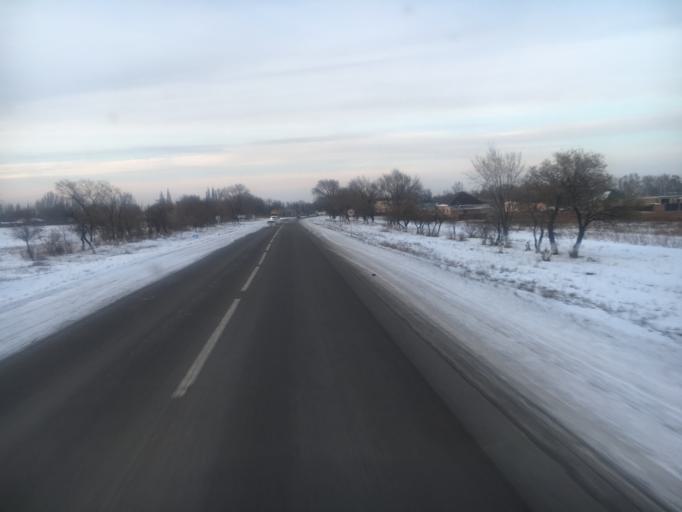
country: KZ
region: Almaty Oblysy
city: Burunday
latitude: 43.3627
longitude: 76.6428
